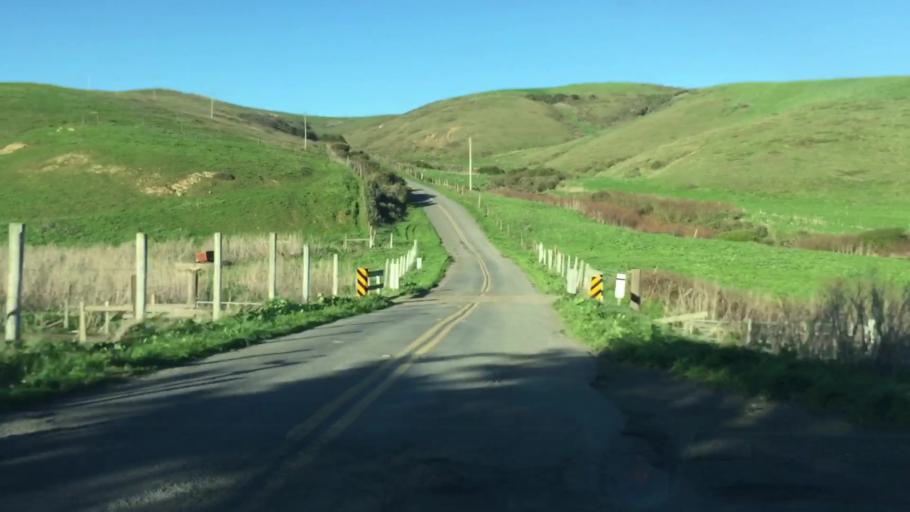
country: US
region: California
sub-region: Marin County
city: Inverness
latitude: 38.1608
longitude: -122.9379
